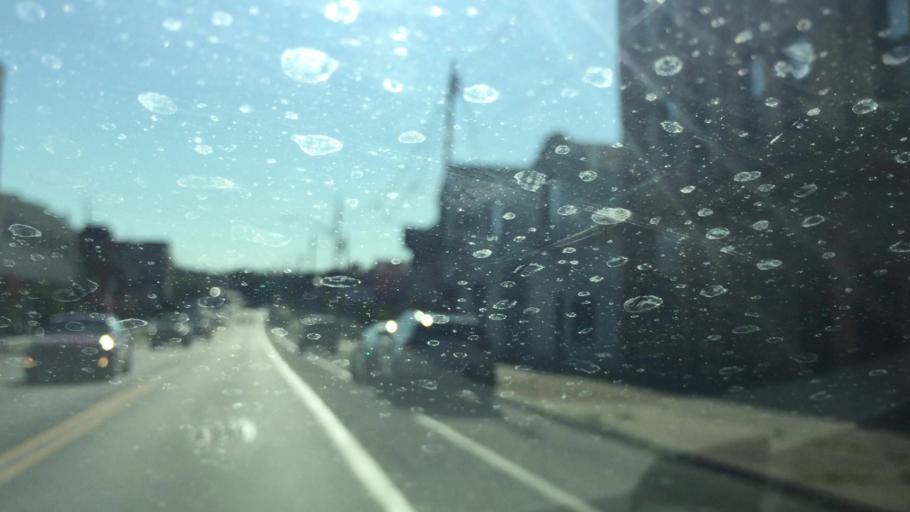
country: US
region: Pennsylvania
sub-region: Allegheny County
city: Bloomfield
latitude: 40.4630
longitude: -79.9563
